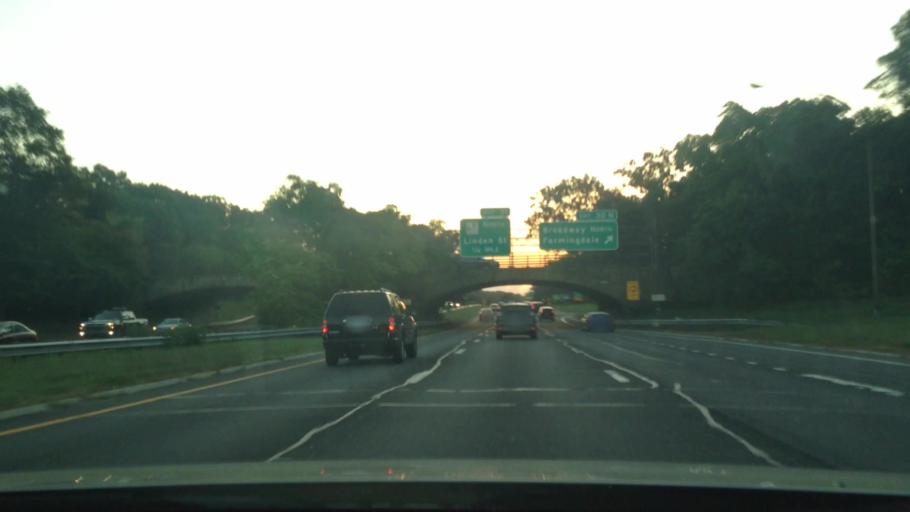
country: US
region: New York
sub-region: Nassau County
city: North Massapequa
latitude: 40.7058
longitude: -73.4625
